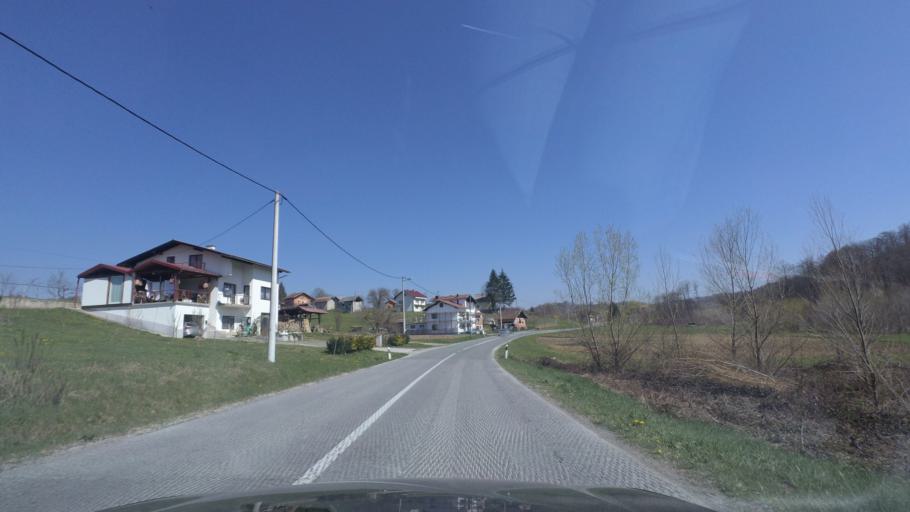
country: HR
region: Karlovacka
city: Vojnic
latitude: 45.3394
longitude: 15.7328
